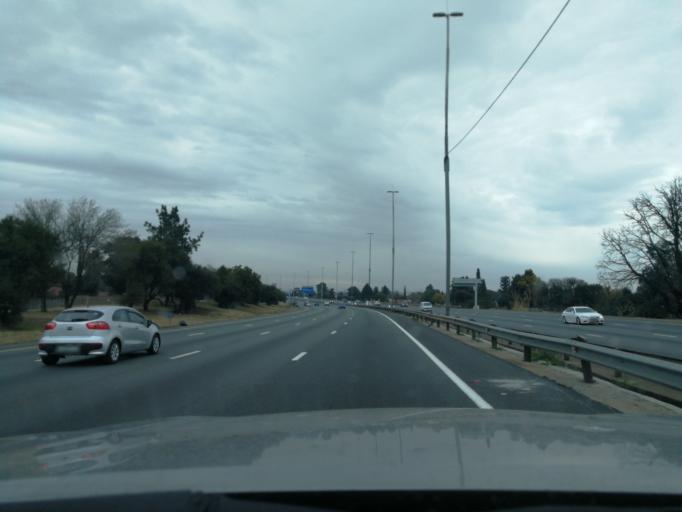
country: ZA
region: Gauteng
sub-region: Ekurhuleni Metropolitan Municipality
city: Germiston
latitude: -26.2739
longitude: 28.1492
